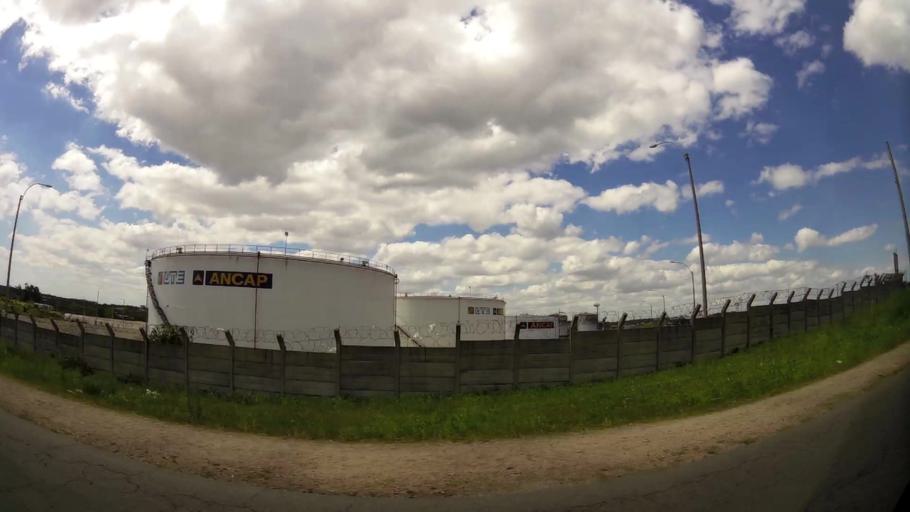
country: UY
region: Canelones
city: La Paz
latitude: -34.8236
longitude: -56.2448
